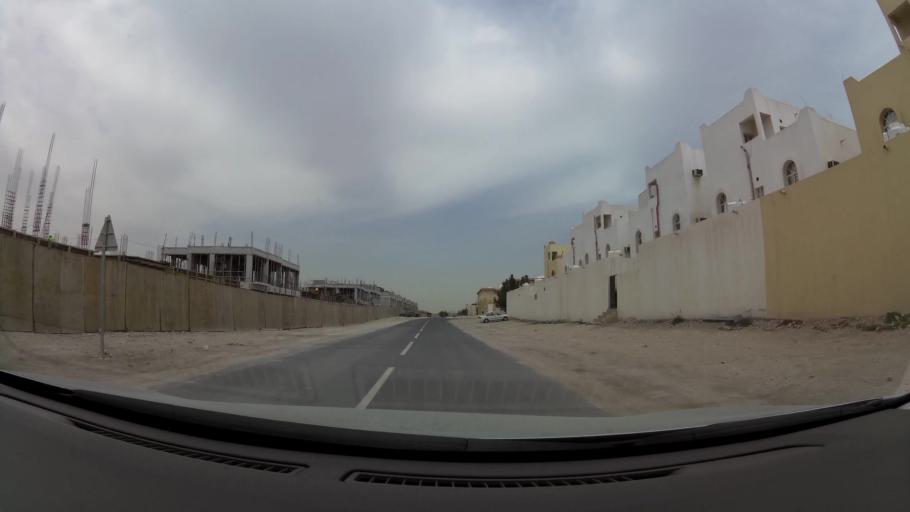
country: QA
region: Baladiyat ar Rayyan
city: Ar Rayyan
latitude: 25.2923
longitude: 51.4558
